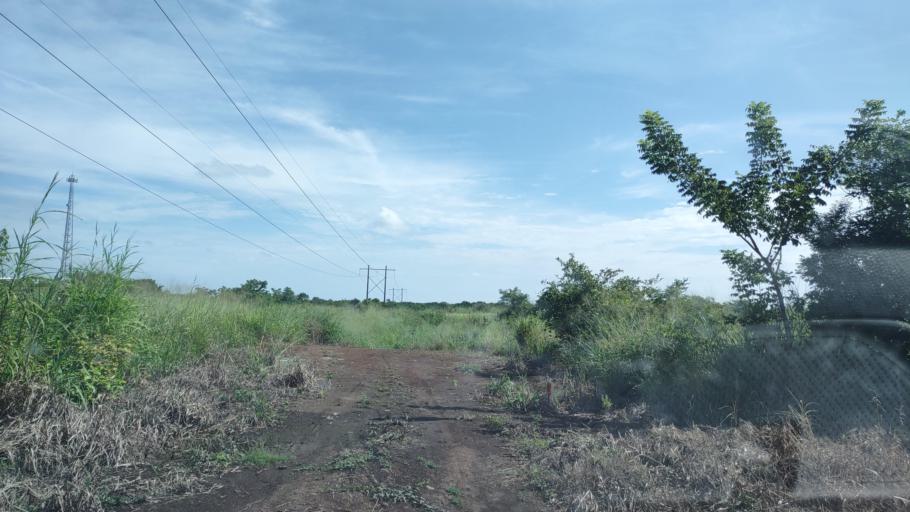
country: MX
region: Veracruz
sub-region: Martinez de la Torre
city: La Union Paso Largo
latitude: 20.1276
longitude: -96.9916
